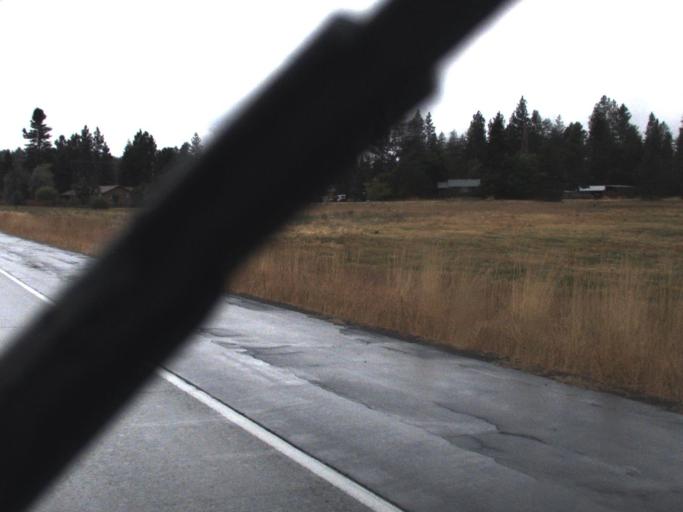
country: US
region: Washington
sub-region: Spokane County
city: Spokane
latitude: 47.5467
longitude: -117.3977
